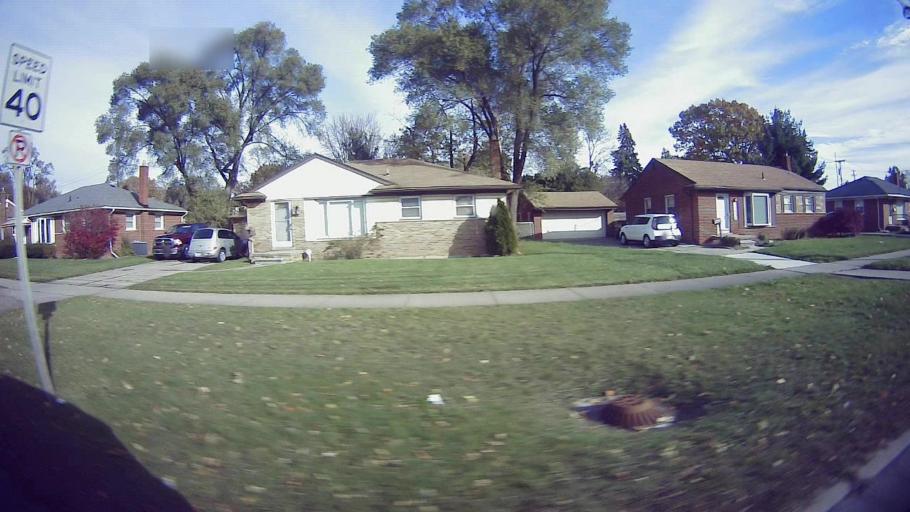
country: US
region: Michigan
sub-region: Wayne County
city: Redford
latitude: 42.3855
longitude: -83.2952
